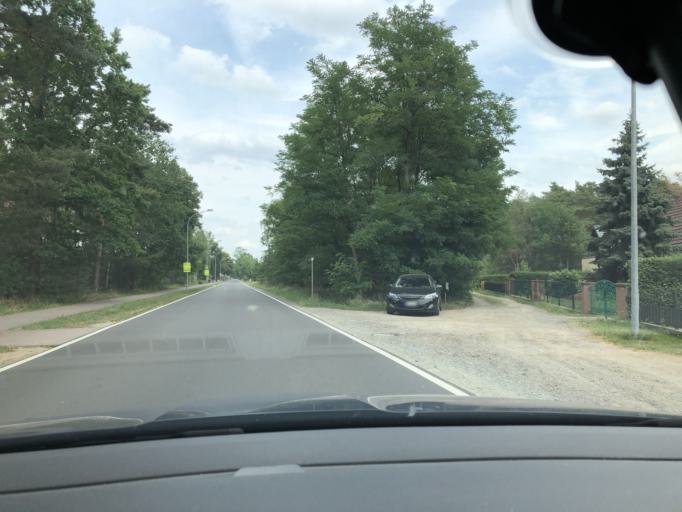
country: DE
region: Brandenburg
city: Kasel-Golzig
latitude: 51.9836
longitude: 13.7718
